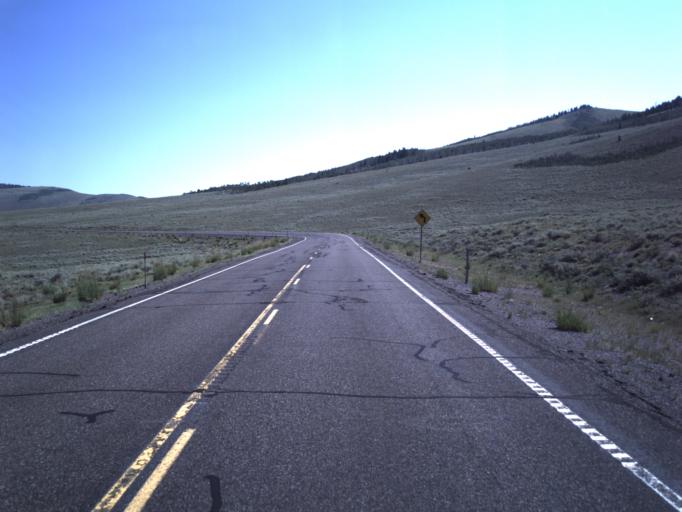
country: US
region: Utah
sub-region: Wayne County
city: Loa
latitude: 38.5594
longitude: -111.5038
